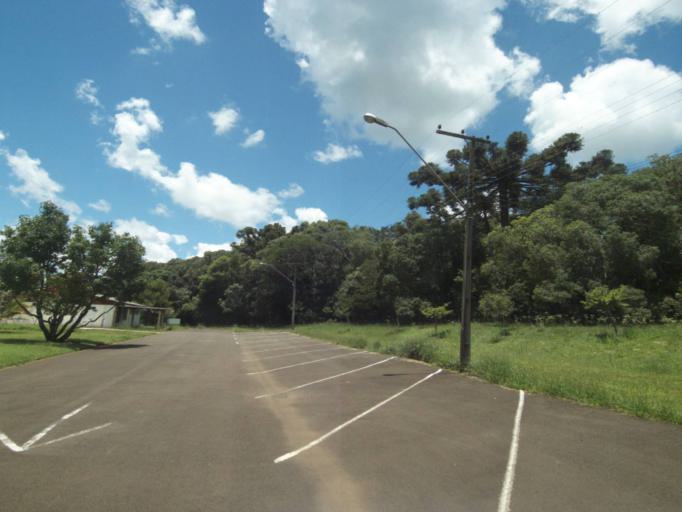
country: BR
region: Parana
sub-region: Pinhao
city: Pinhao
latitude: -25.7927
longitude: -52.0811
